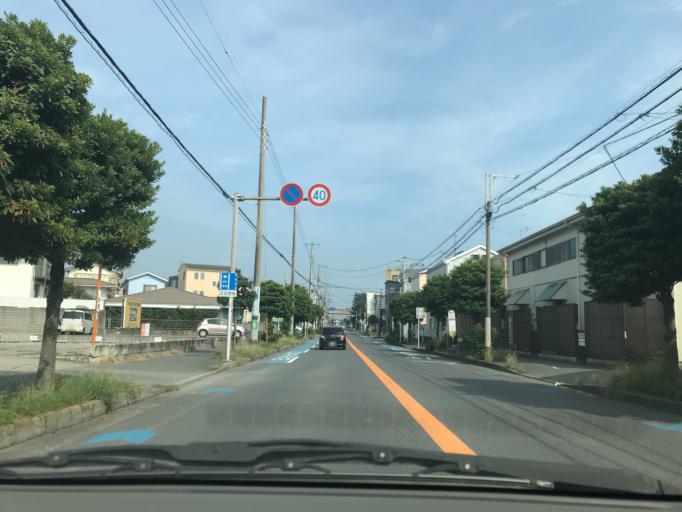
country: JP
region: Kanagawa
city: Chigasaki
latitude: 35.3255
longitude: 139.4291
